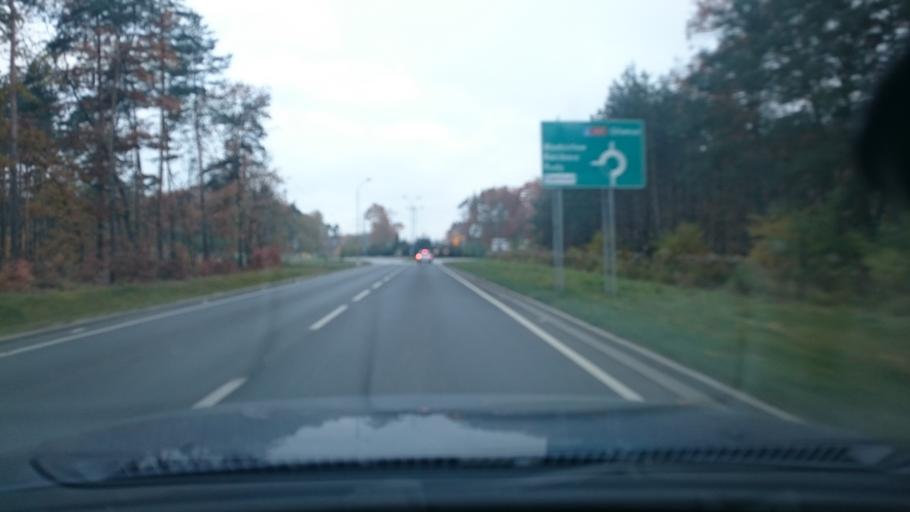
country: PL
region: Silesian Voivodeship
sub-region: Rybnik
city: Rybnik
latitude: 50.1140
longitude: 18.5555
